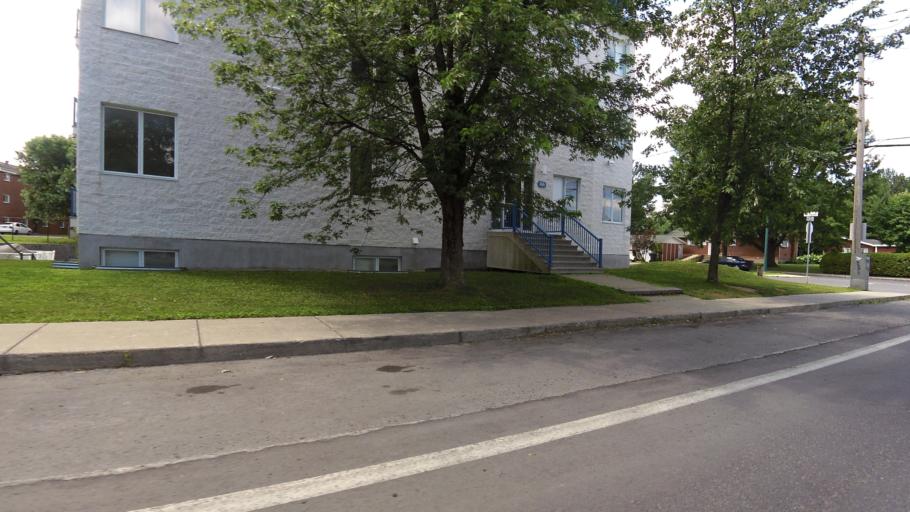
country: CA
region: Quebec
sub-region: Monteregie
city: Saint-Jean-sur-Richelieu
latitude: 45.2944
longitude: -73.2628
